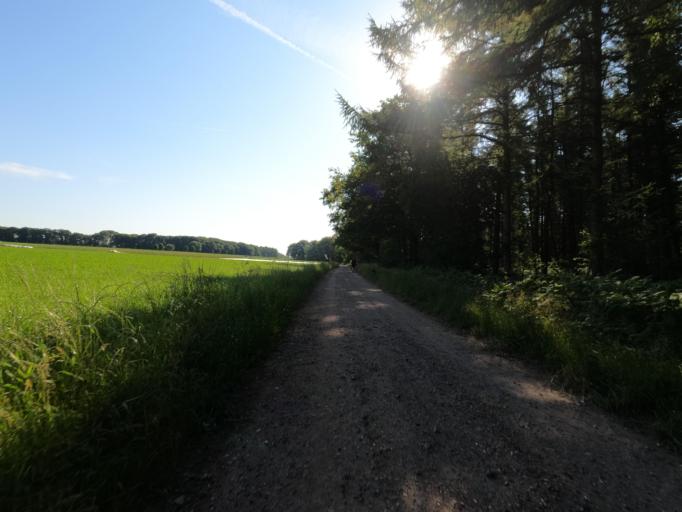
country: NL
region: Limburg
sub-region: Gemeente Roerdalen
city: Vlodrop
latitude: 51.1213
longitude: 6.0669
